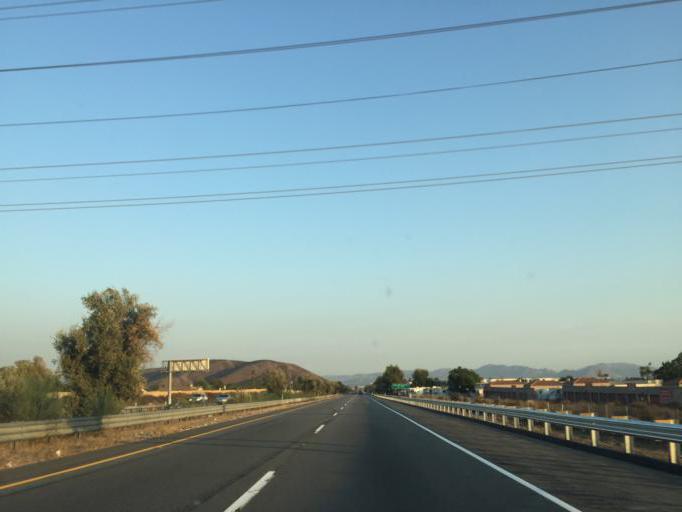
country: US
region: California
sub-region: San Bernardino County
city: Muscoy
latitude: 34.1782
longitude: -117.3454
